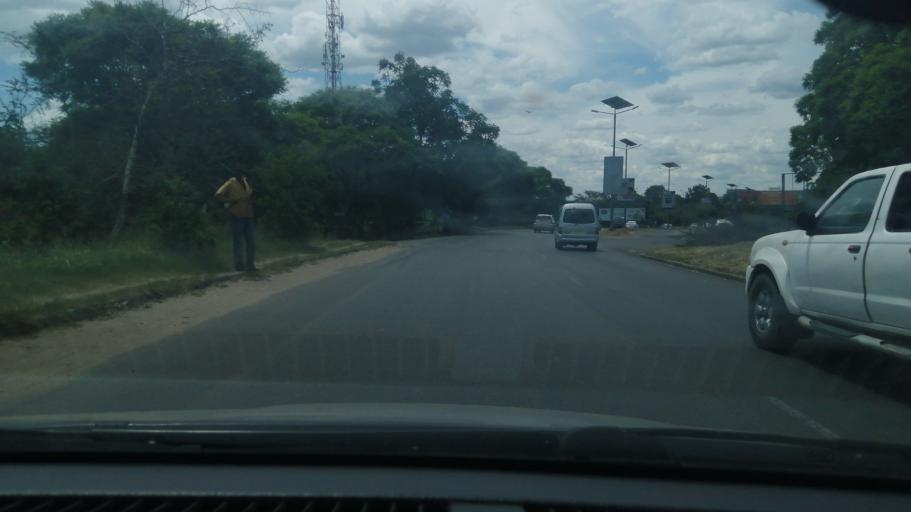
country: ZW
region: Harare
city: Harare
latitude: -17.8358
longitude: 31.1041
